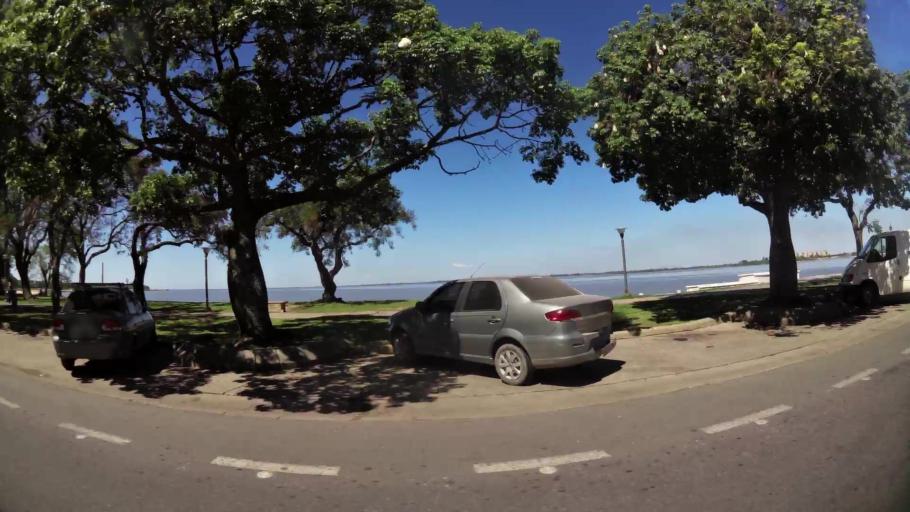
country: AR
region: Santa Fe
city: Santa Fe de la Vera Cruz
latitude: -31.6274
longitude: -60.6787
